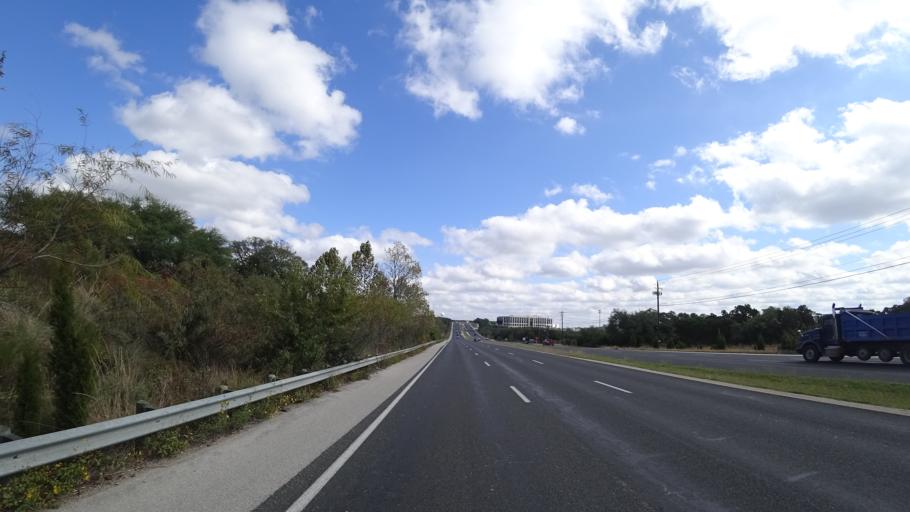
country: US
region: Texas
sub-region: Travis County
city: Barton Creek
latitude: 30.2568
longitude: -97.8785
